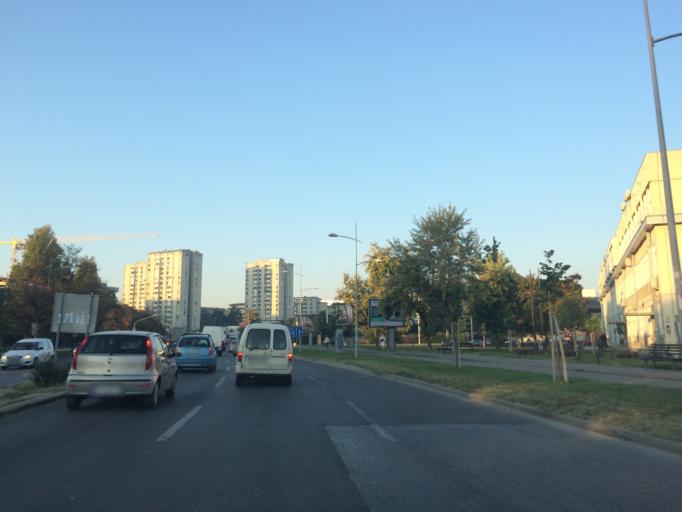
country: RS
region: Autonomna Pokrajina Vojvodina
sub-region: Juznobacki Okrug
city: Novi Sad
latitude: 45.2474
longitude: 19.8489
